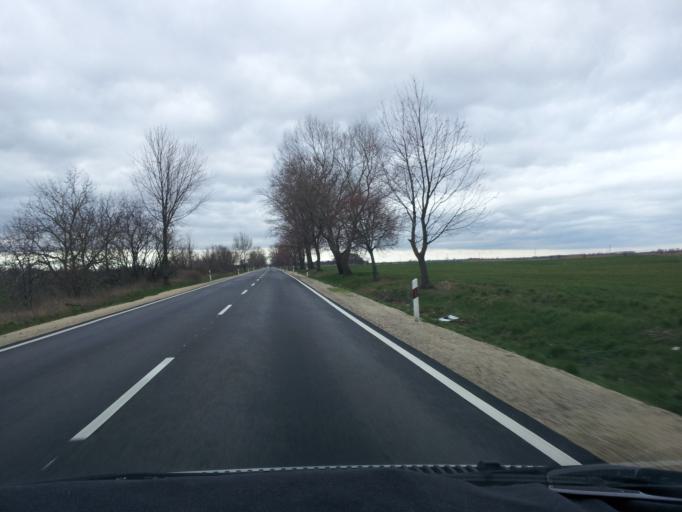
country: HU
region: Gyor-Moson-Sopron
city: Beled
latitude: 47.4537
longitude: 17.0872
